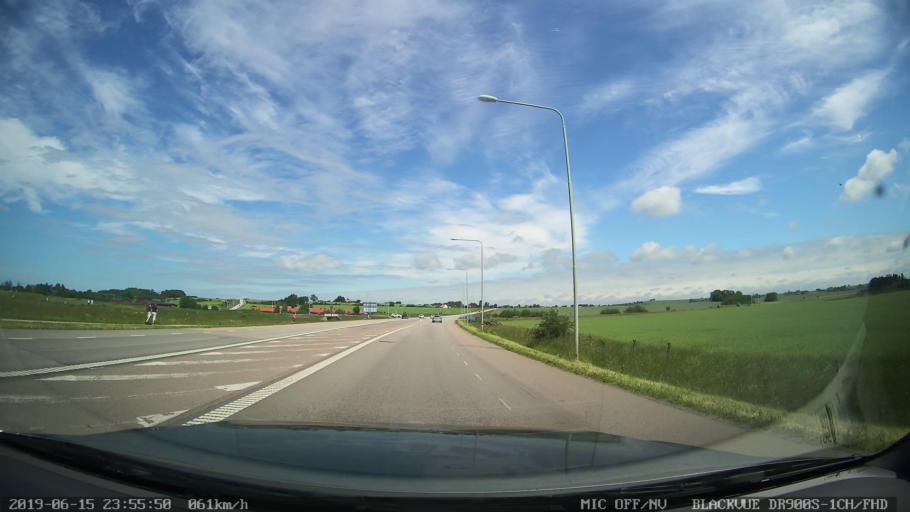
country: SE
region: Skane
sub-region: Landskrona
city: Landskrona
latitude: 55.9053
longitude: 12.8259
